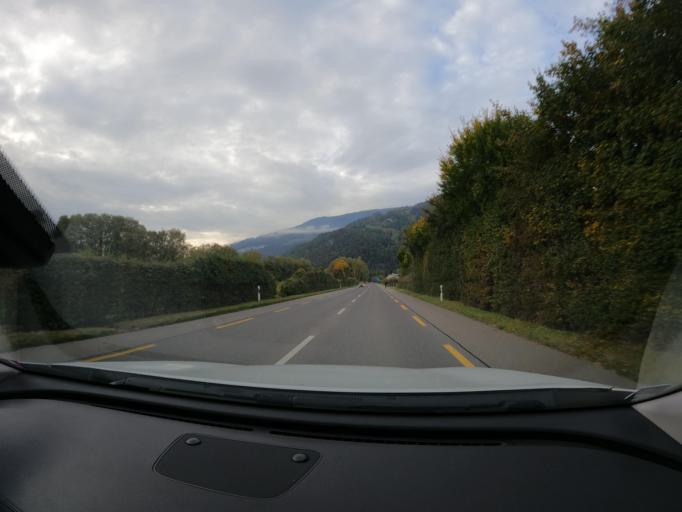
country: CH
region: Bern
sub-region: Interlaken-Oberhasli District
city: Unterseen
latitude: 46.6773
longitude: 7.8293
